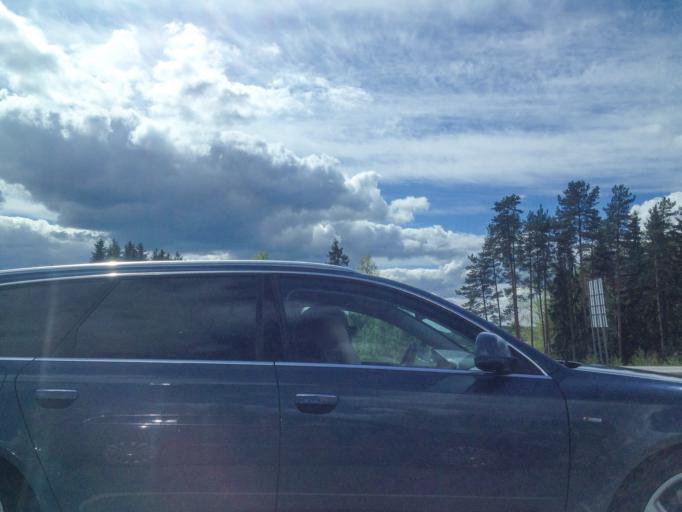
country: FI
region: Pirkanmaa
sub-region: Etelae-Pirkanmaa
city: Viiala
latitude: 61.2676
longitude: 23.8245
